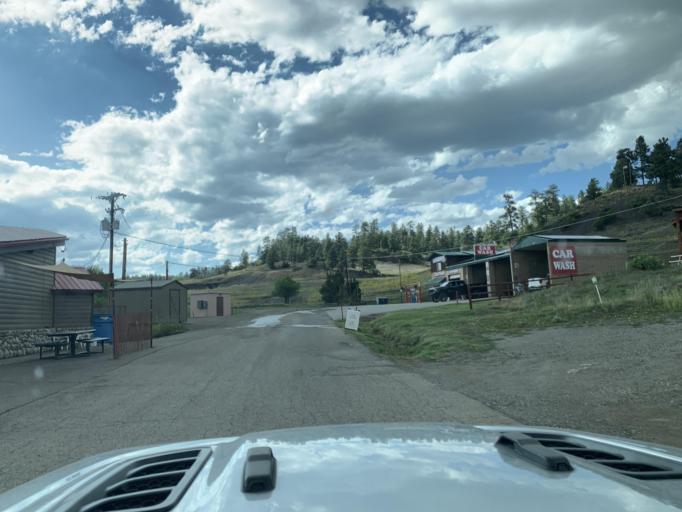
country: US
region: Colorado
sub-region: Archuleta County
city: Pagosa Springs
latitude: 37.2672
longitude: -107.0192
